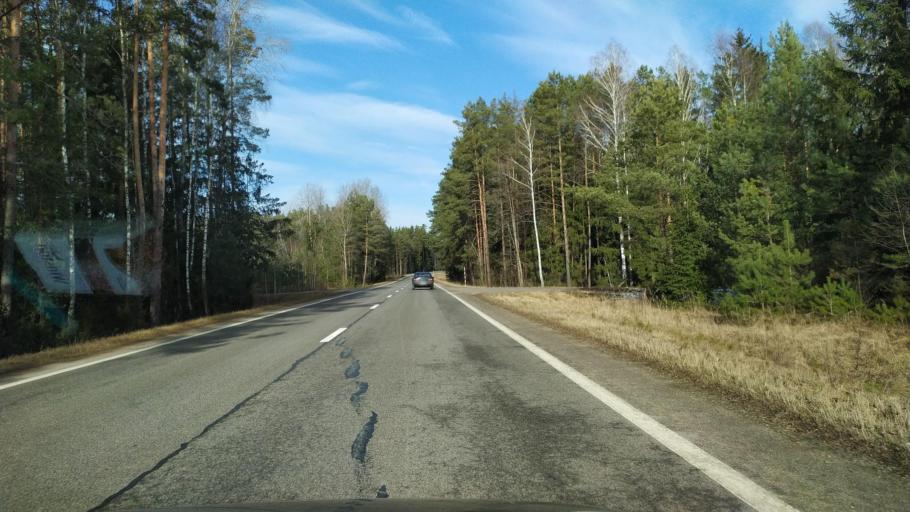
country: BY
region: Brest
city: Pruzhany
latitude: 52.4924
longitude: 24.1711
